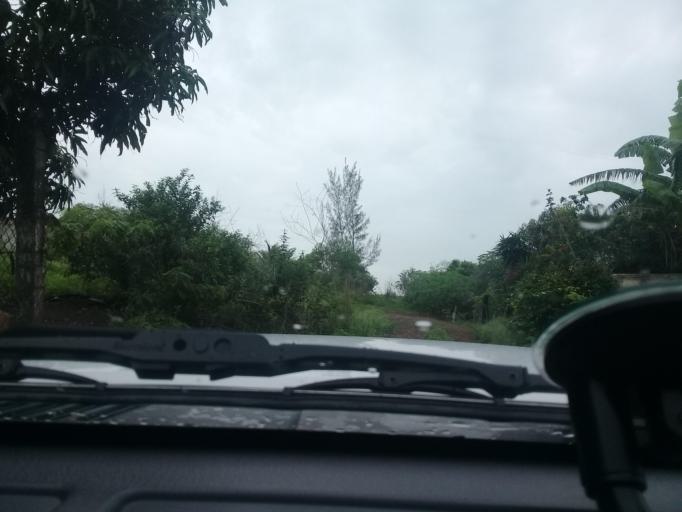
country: MX
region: Veracruz
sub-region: Puente Nacional
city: Cabezas
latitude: 19.3654
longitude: -96.4006
